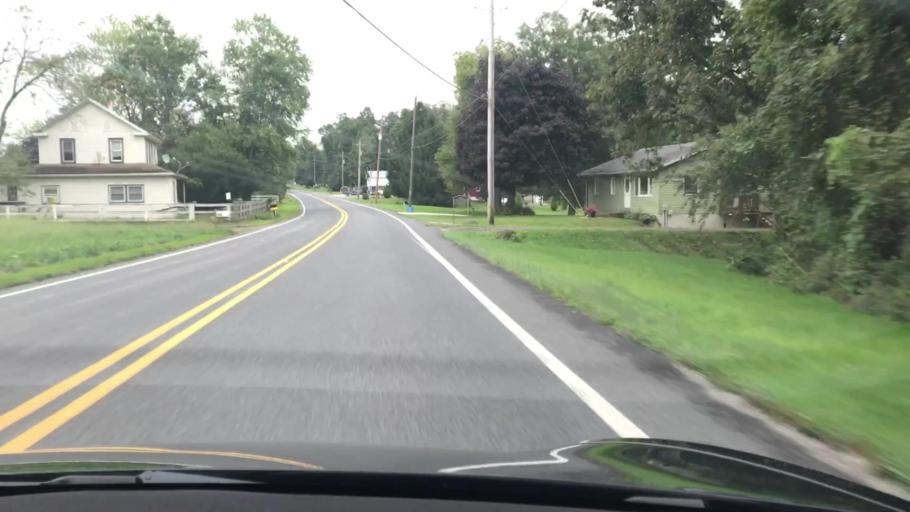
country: US
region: Pennsylvania
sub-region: Adams County
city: Lake Meade
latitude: 39.9503
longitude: -77.1134
